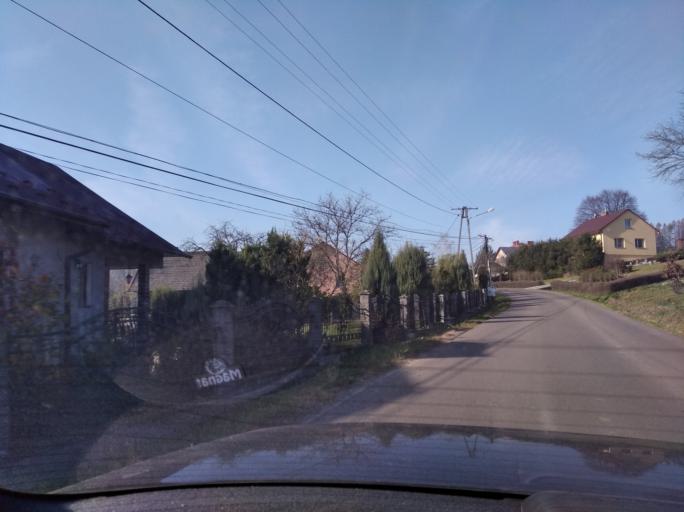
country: PL
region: Subcarpathian Voivodeship
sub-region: Powiat strzyzowski
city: Wisniowa
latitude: 49.8714
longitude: 21.6323
